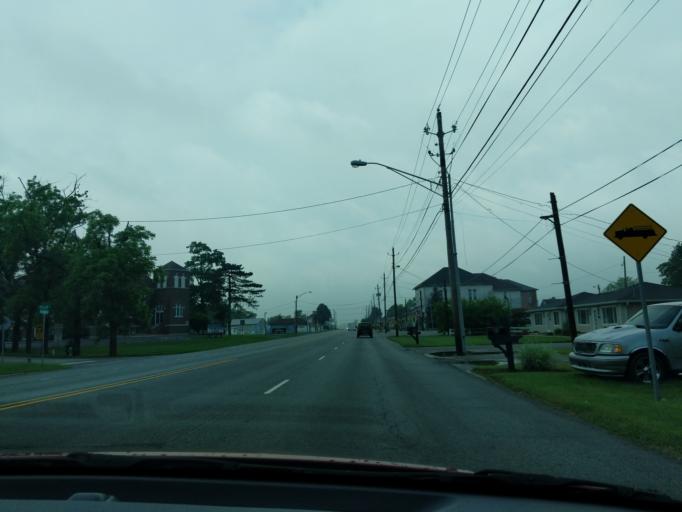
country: US
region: Indiana
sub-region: Hancock County
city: McCordsville
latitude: 39.8945
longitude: -85.9224
